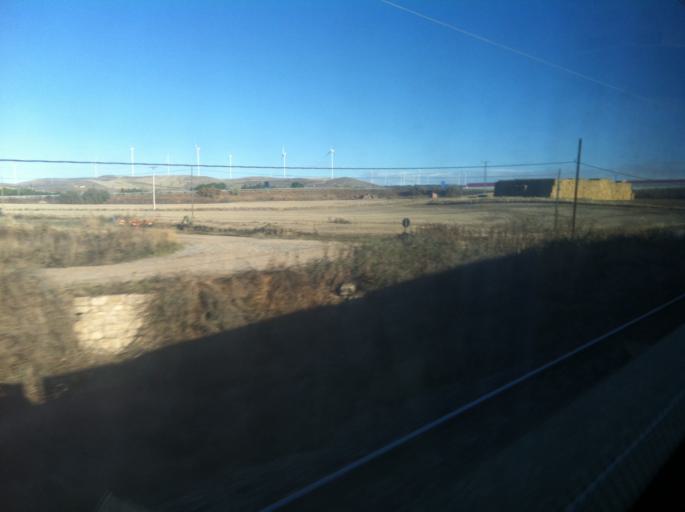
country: ES
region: Castille and Leon
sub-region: Provincia de Burgos
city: Villazopeque
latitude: 42.1988
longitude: -4.0183
